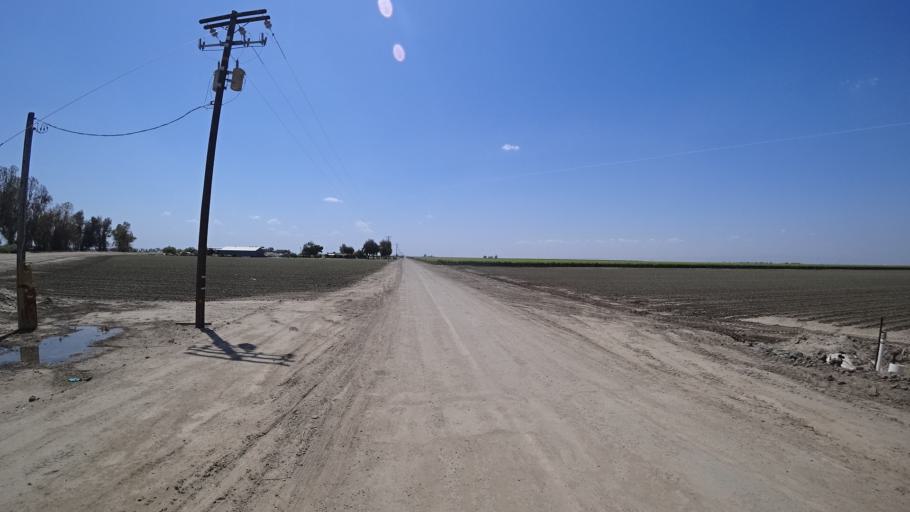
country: US
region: California
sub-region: Kings County
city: Stratford
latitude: 36.2061
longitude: -119.8514
